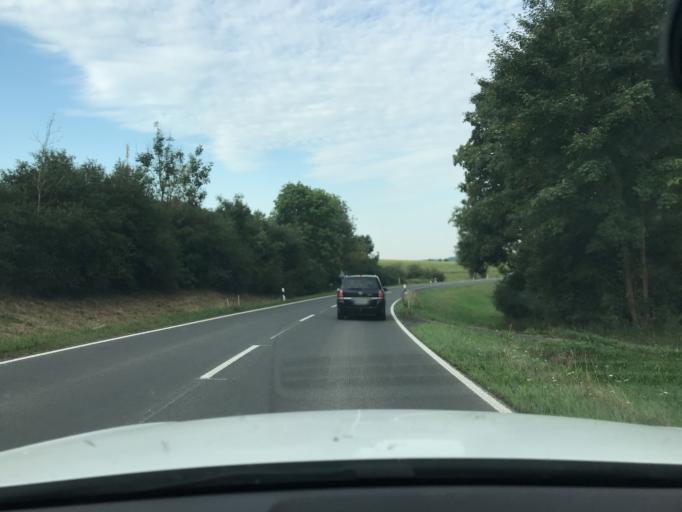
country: DE
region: Bavaria
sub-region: Upper Franconia
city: Pegnitz
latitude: 49.7574
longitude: 11.5609
